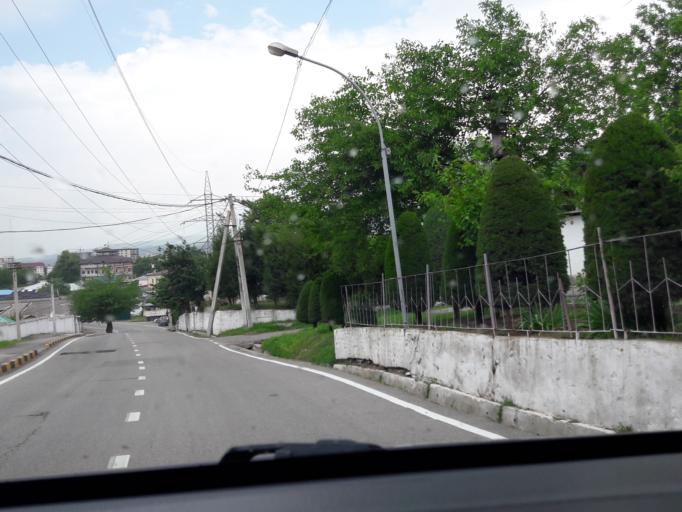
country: TJ
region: Dushanbe
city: Dushanbe
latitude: 38.5802
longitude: 68.8056
